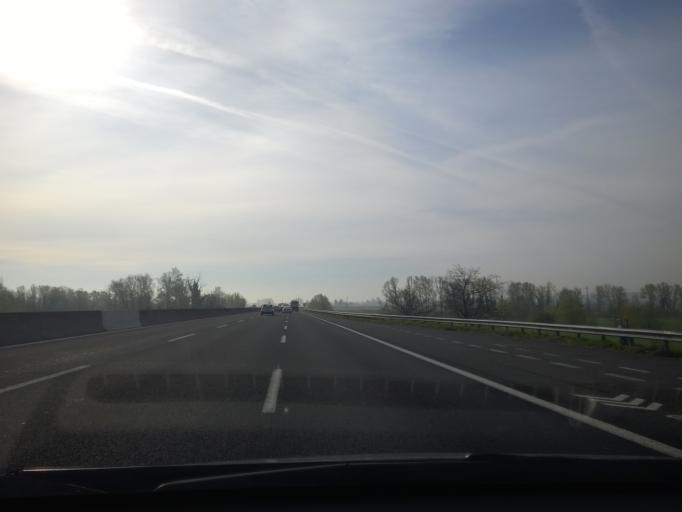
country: IT
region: Emilia-Romagna
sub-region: Provincia di Bologna
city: Toscanella
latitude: 44.4188
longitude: 11.6230
